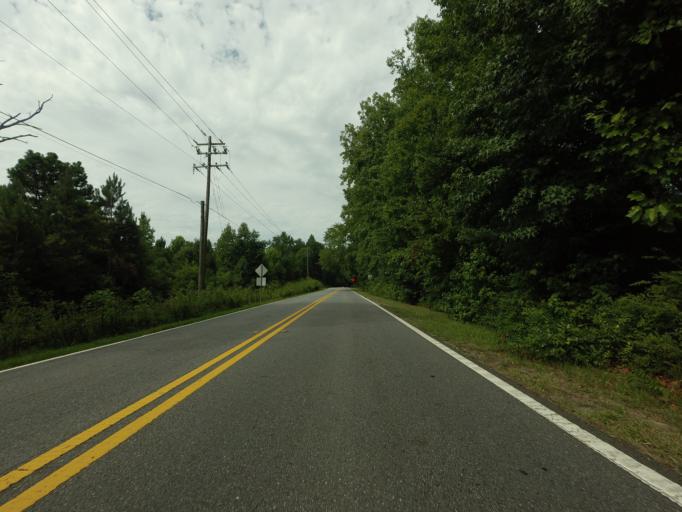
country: US
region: Georgia
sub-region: Gwinnett County
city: Duluth
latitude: 34.0425
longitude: -84.1416
